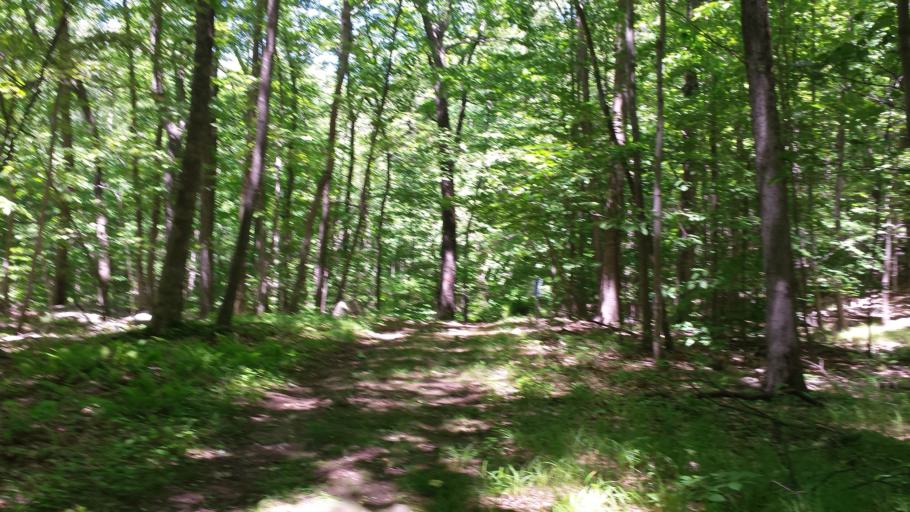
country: US
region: New York
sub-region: Westchester County
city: Pound Ridge
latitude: 41.2504
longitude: -73.5831
